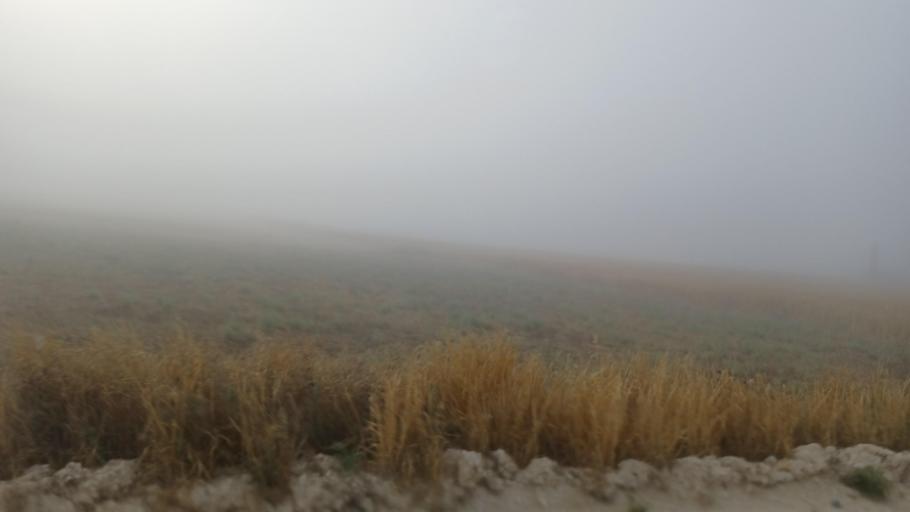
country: CY
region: Ammochostos
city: Acheritou
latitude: 35.0902
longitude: 33.8764
